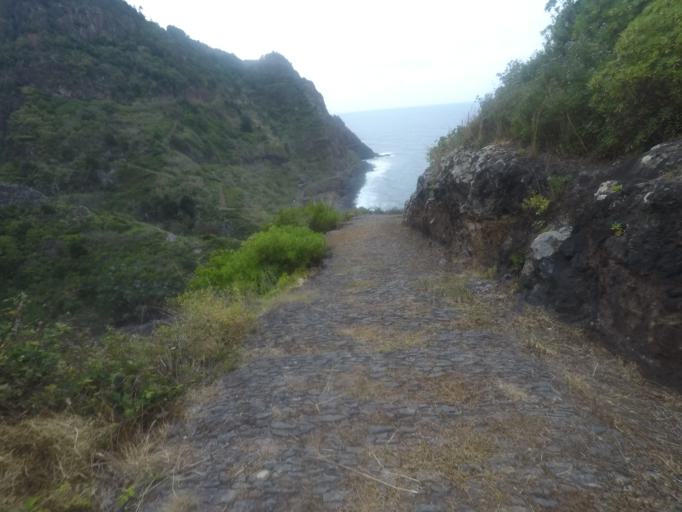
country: PT
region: Madeira
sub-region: Santana
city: Santana
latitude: 32.8283
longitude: -16.8960
